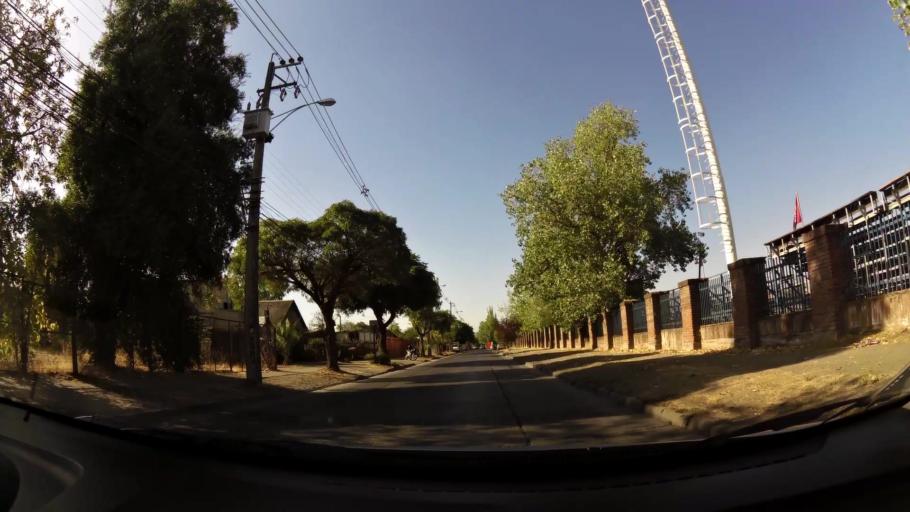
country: CL
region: Maule
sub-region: Provincia de Talca
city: Talca
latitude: -35.4427
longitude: -71.6668
